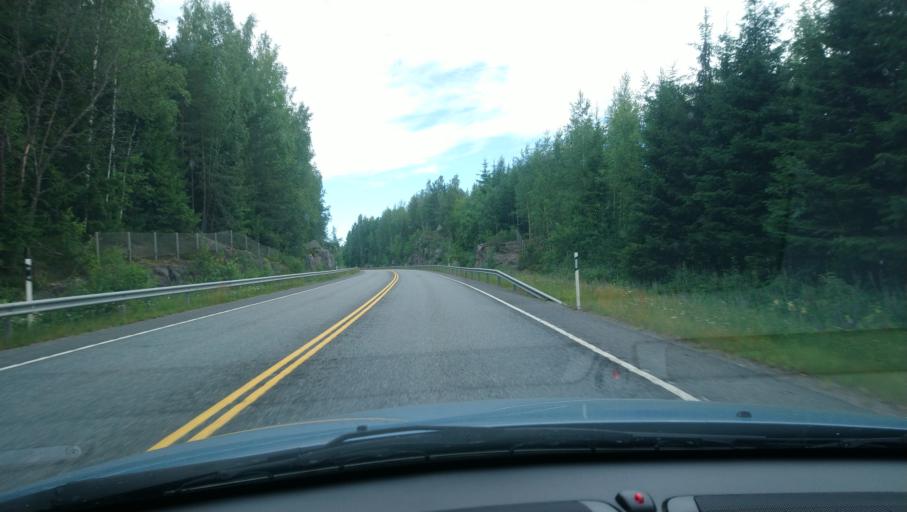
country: FI
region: Uusimaa
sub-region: Porvoo
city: Porvoo
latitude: 60.4240
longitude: 25.5798
